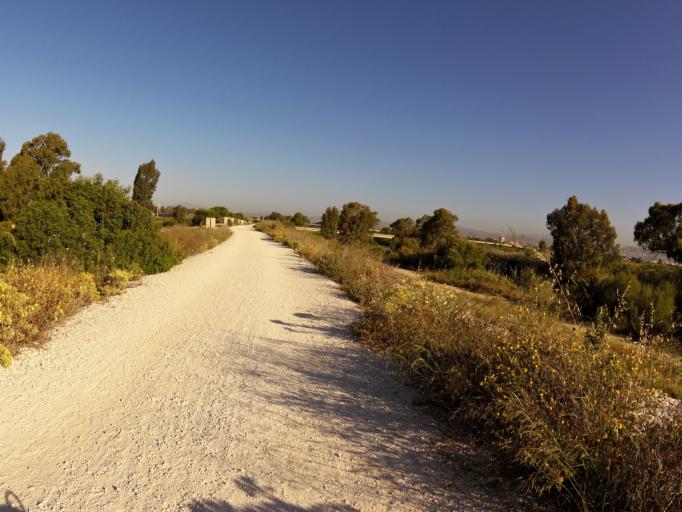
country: ES
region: Andalusia
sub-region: Provincia de Malaga
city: Malaga
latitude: 36.6708
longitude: -4.4607
